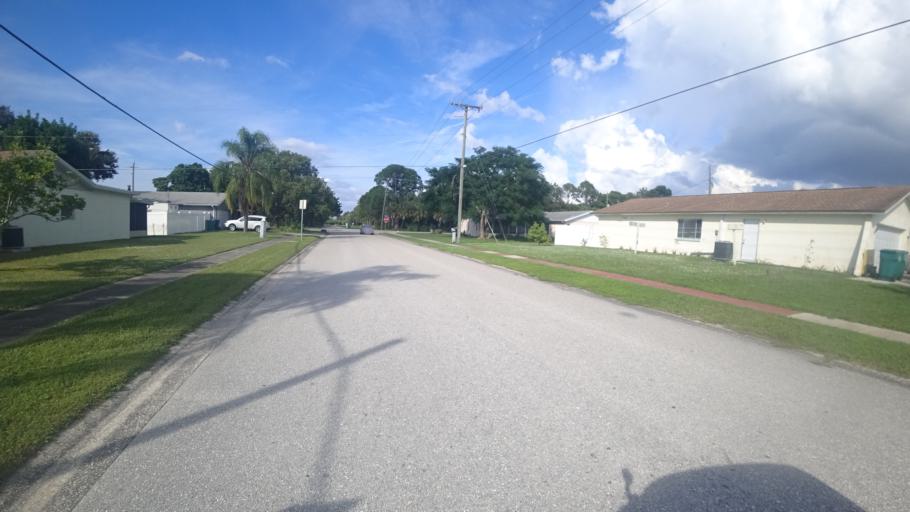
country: US
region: Florida
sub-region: Manatee County
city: Palmetto
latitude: 27.5280
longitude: -82.5933
